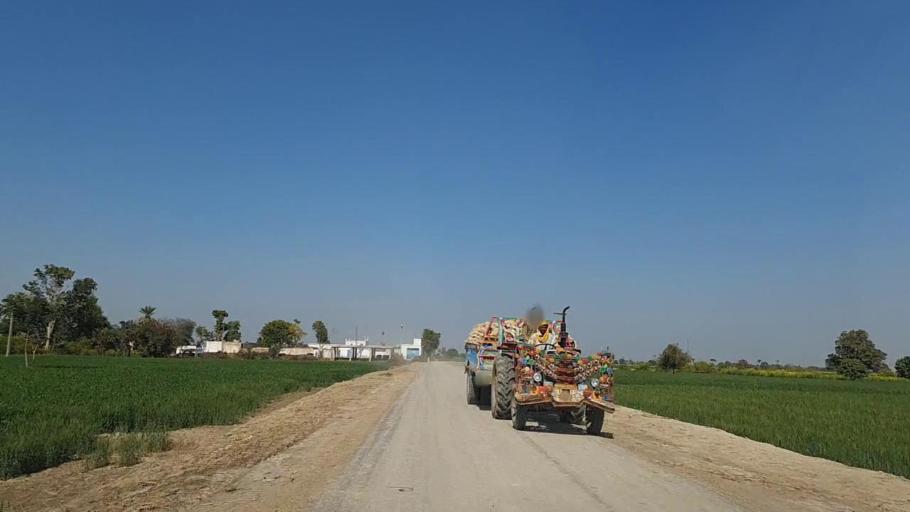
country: PK
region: Sindh
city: Nawabshah
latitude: 26.2585
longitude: 68.4515
